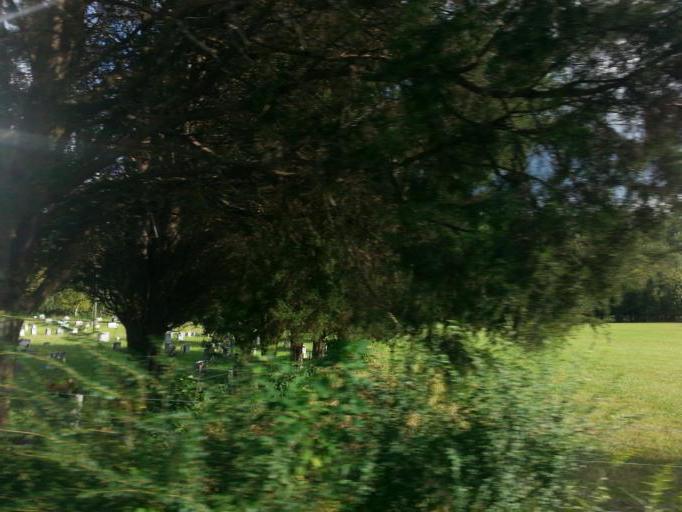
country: US
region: Tennessee
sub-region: Knox County
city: Mascot
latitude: 36.0694
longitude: -83.8449
